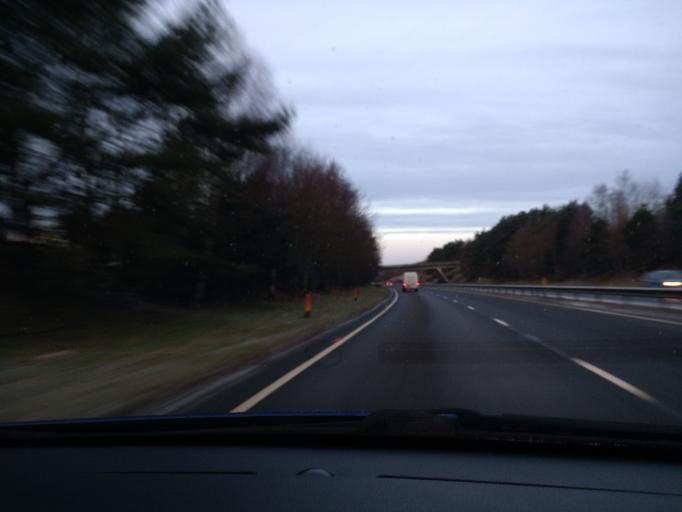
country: GB
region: England
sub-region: Northumberland
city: Corbridge
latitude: 54.9823
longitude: -1.9953
